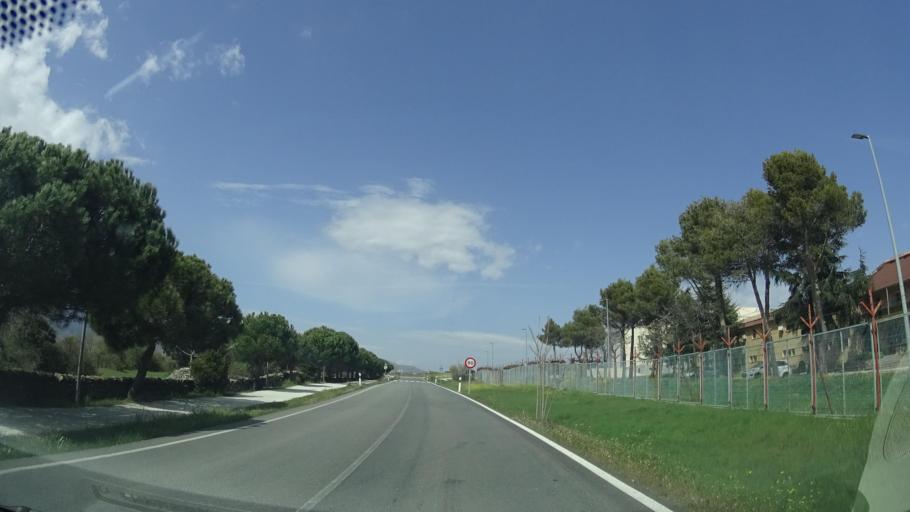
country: ES
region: Madrid
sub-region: Provincia de Madrid
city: Colmenar Viejo
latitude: 40.6985
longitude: -3.7677
